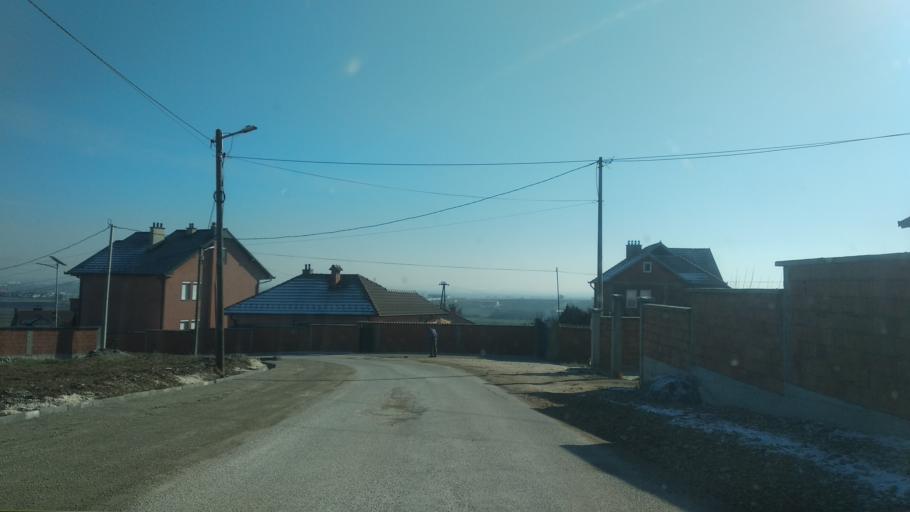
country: XK
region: Pristina
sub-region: Komuna e Gracanices
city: Glanica
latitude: 42.6069
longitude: 21.0272
